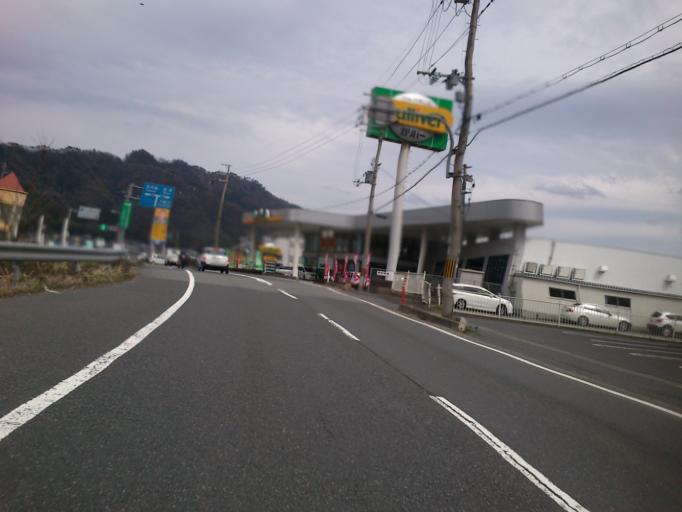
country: JP
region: Kyoto
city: Miyazu
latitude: 35.5336
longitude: 135.1224
